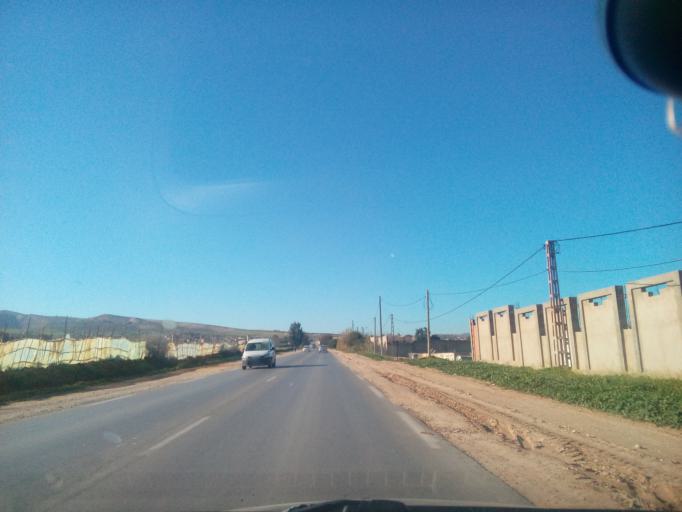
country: DZ
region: Relizane
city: Relizane
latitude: 35.9018
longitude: 0.5254
